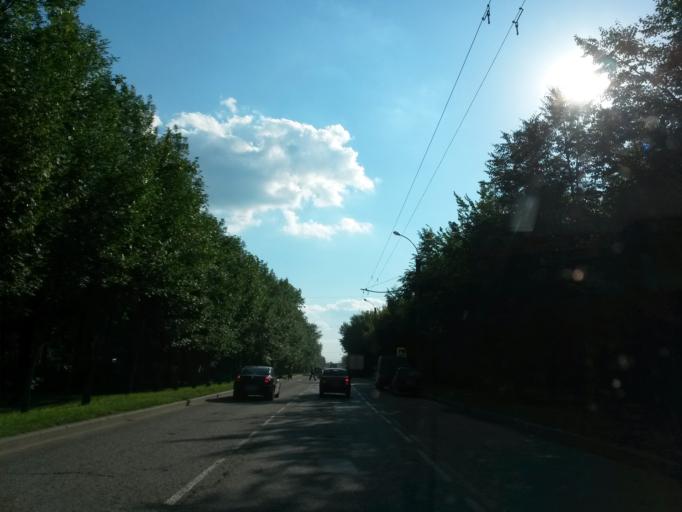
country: RU
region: Ivanovo
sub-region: Gorod Ivanovo
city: Ivanovo
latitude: 56.9619
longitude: 41.0126
